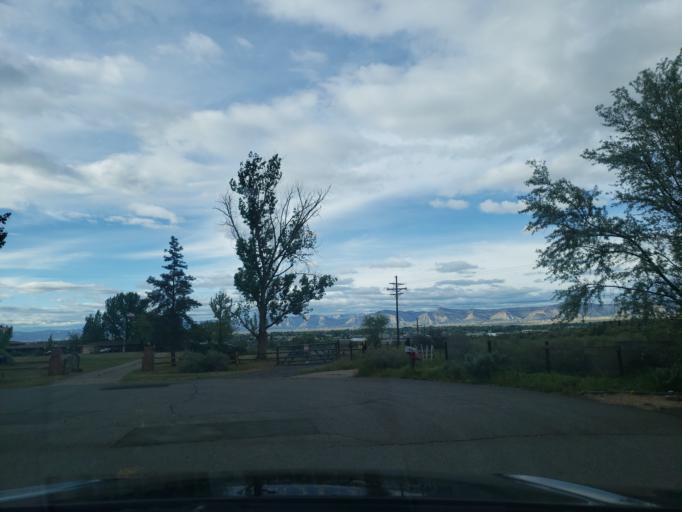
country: US
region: Colorado
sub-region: Mesa County
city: Redlands
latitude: 39.1031
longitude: -108.6615
